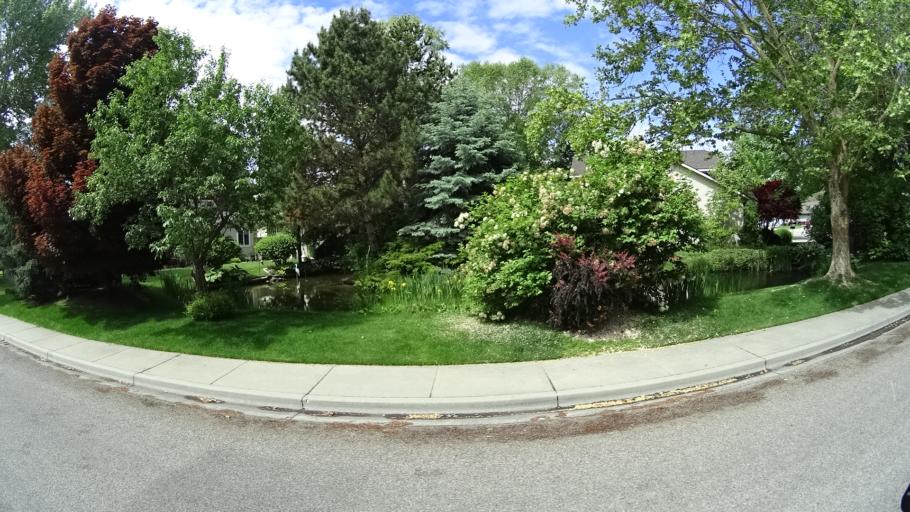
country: US
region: Idaho
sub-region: Ada County
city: Boise
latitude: 43.5787
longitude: -116.1637
